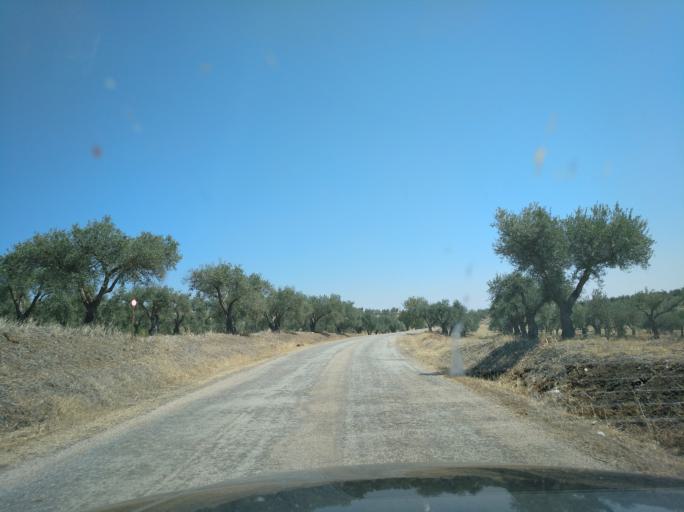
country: PT
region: Portalegre
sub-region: Campo Maior
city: Campo Maior
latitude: 38.9858
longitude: -7.1017
